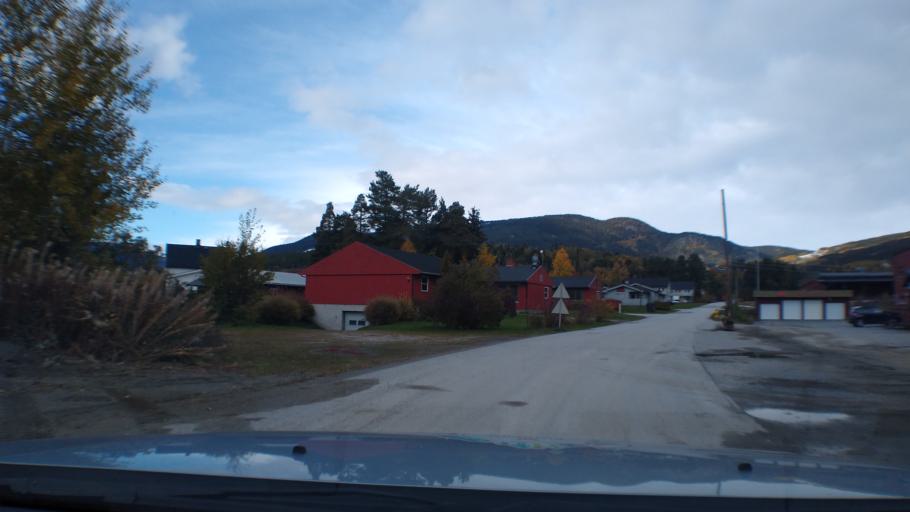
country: NO
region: Oppland
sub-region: Ringebu
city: Ringebu
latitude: 61.5256
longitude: 10.1362
